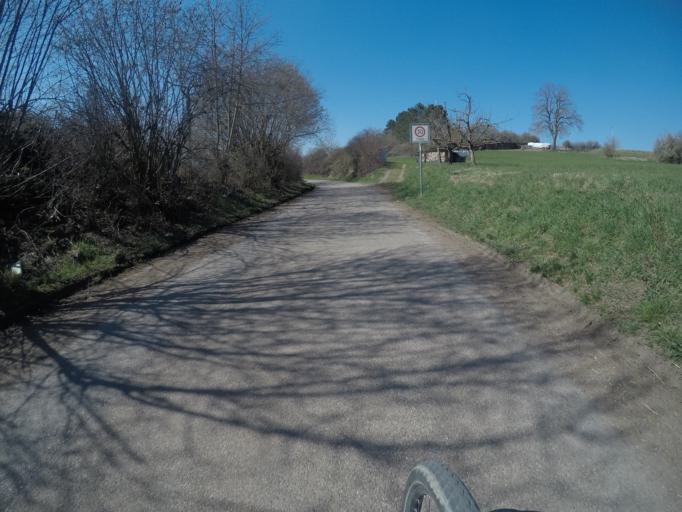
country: DE
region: Baden-Wuerttemberg
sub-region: Regierungsbezirk Stuttgart
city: Aidlingen
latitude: 48.7099
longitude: 8.9223
